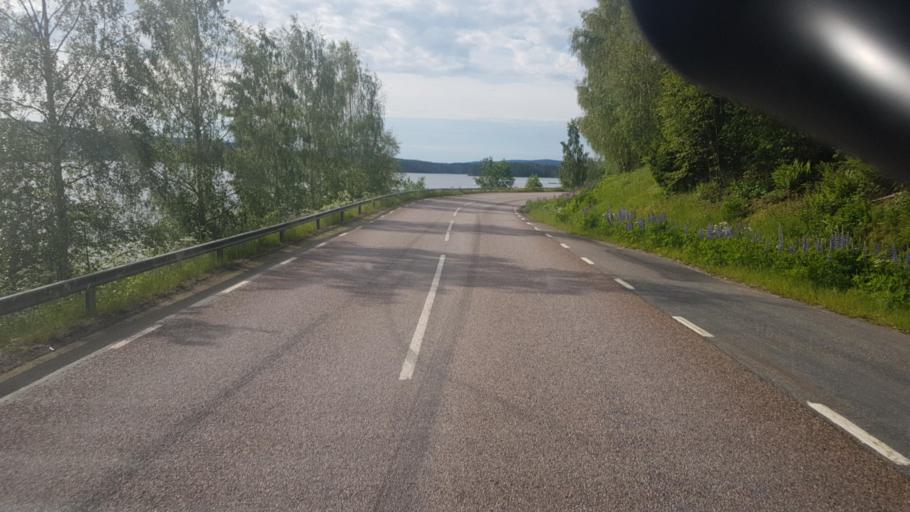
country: SE
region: Vaermland
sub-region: Arvika Kommun
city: Arvika
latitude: 59.8089
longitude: 12.5590
